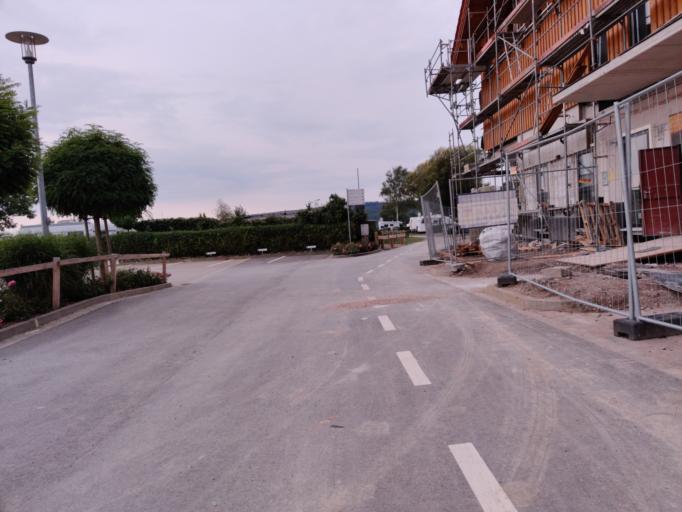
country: DE
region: Lower Saxony
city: Hehlen
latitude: 52.0185
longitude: 9.4262
